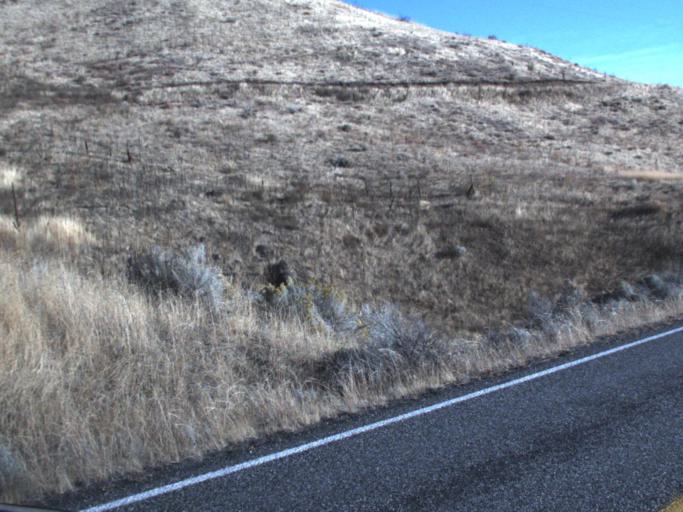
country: US
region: Washington
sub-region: Okanogan County
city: Coulee Dam
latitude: 47.9989
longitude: -118.6891
